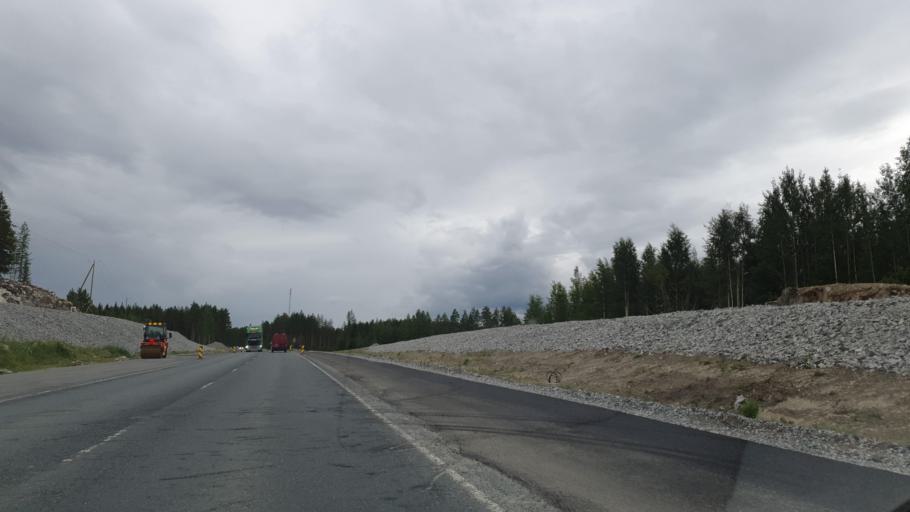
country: FI
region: Northern Savo
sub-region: Ylae-Savo
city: Lapinlahti
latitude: 63.2822
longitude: 27.4556
